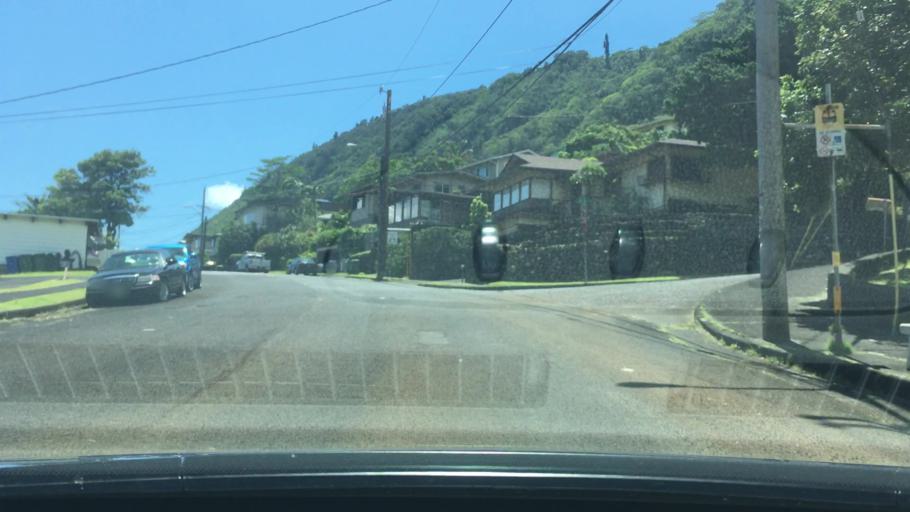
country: US
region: Hawaii
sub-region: Honolulu County
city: Honolulu
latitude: 21.3237
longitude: -157.8048
